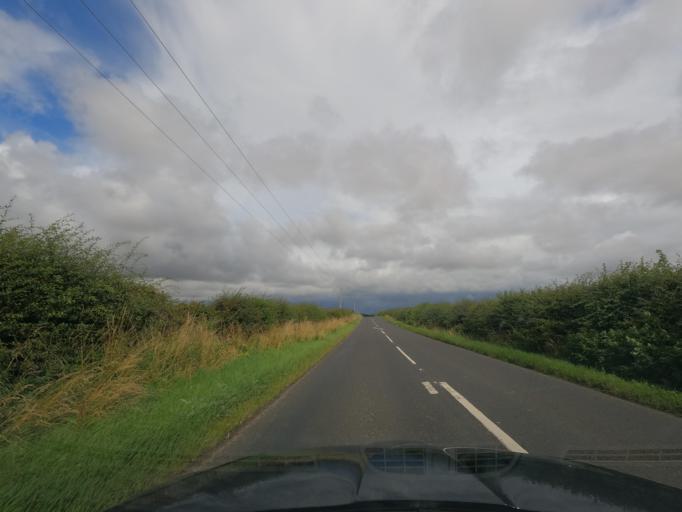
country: GB
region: England
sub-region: Northumberland
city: Ancroft
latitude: 55.6727
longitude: -2.0011
